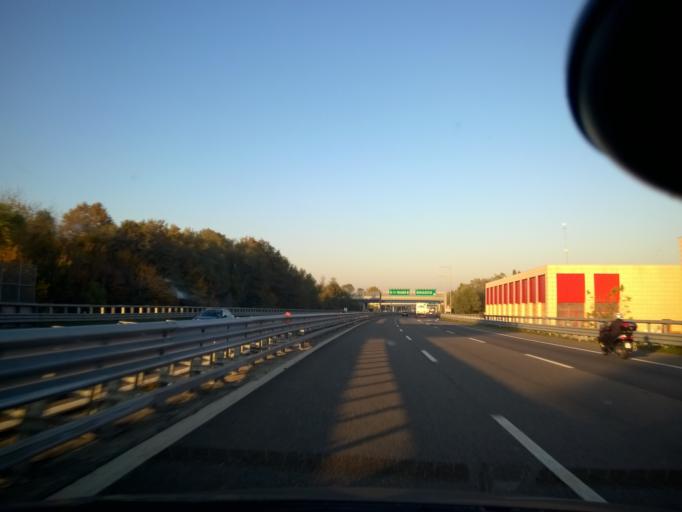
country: IT
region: Lombardy
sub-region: Citta metropolitana di Milano
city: Binasco
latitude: 45.3370
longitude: 9.0963
